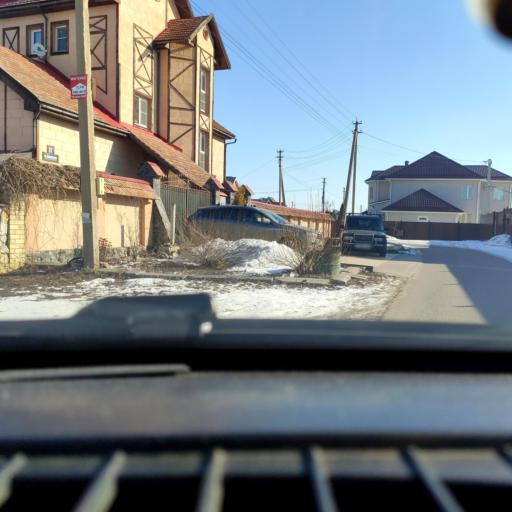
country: RU
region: Voronezj
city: Novaya Usman'
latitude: 51.6636
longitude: 39.3333
